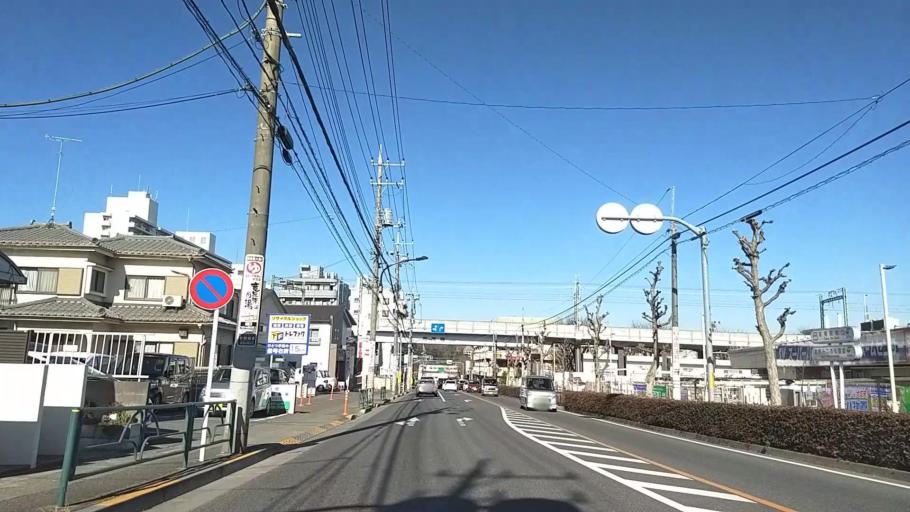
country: JP
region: Tokyo
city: Hachioji
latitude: 35.6406
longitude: 139.2867
